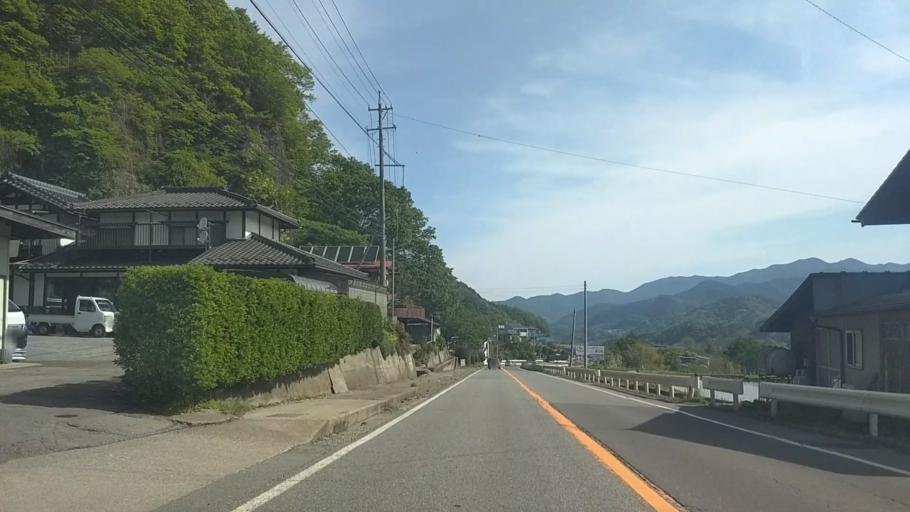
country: JP
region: Nagano
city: Saku
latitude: 36.0727
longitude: 138.4764
